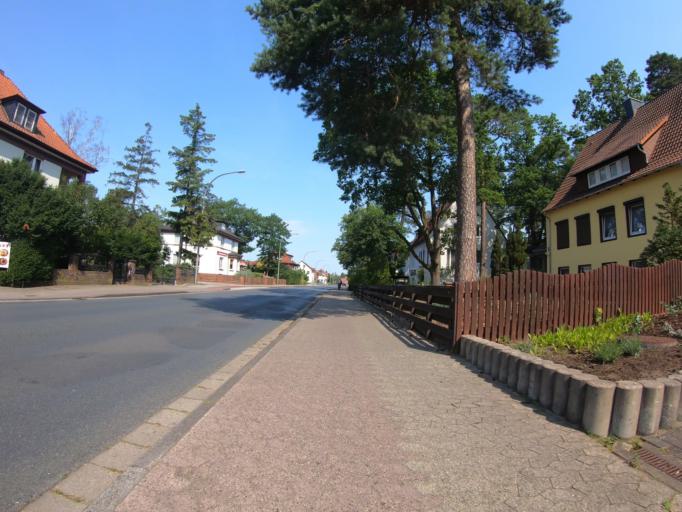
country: DE
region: Lower Saxony
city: Gifhorn
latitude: 52.4777
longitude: 10.5536
